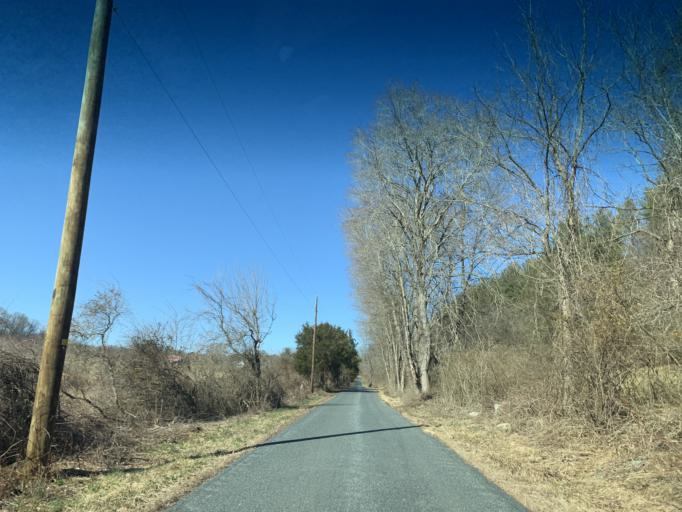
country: US
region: Maryland
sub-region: Harford County
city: Aberdeen
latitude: 39.6198
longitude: -76.2342
